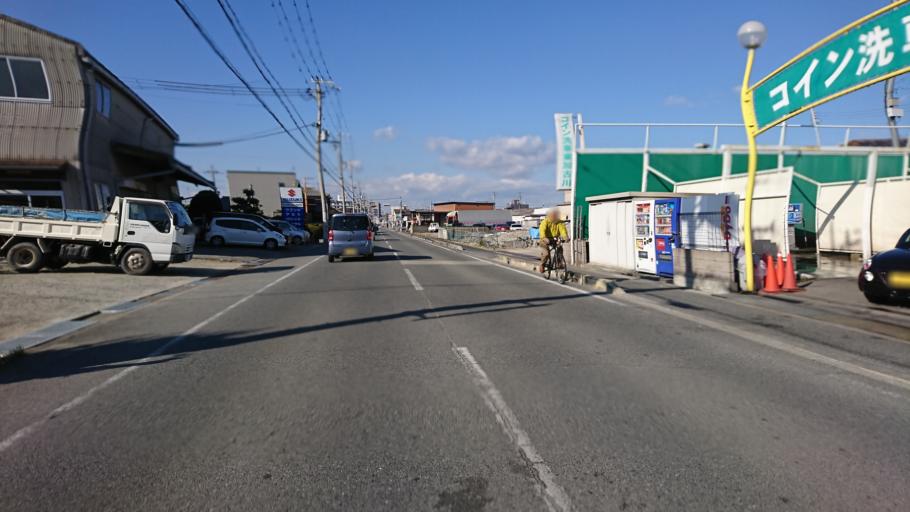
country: JP
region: Hyogo
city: Kakogawacho-honmachi
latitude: 34.7350
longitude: 134.8655
